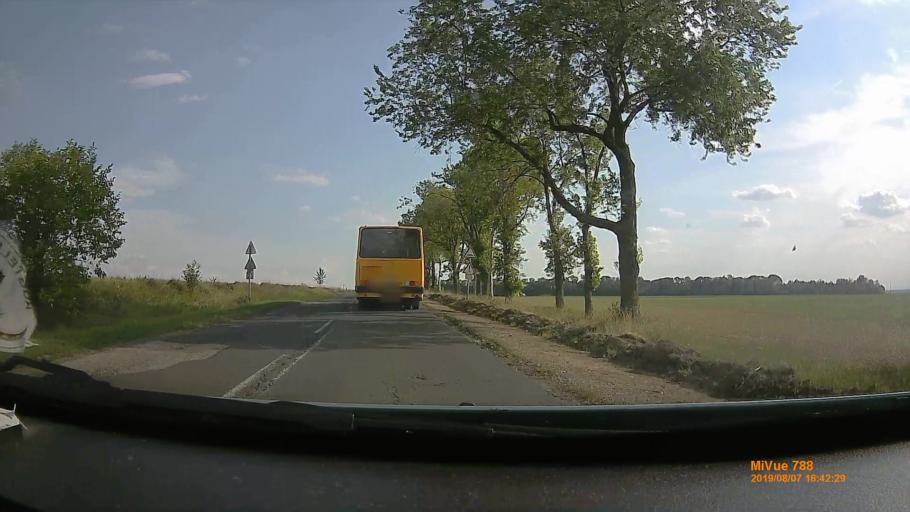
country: HU
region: Borsod-Abauj-Zemplen
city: Abaujszanto
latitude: 48.3689
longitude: 21.2157
